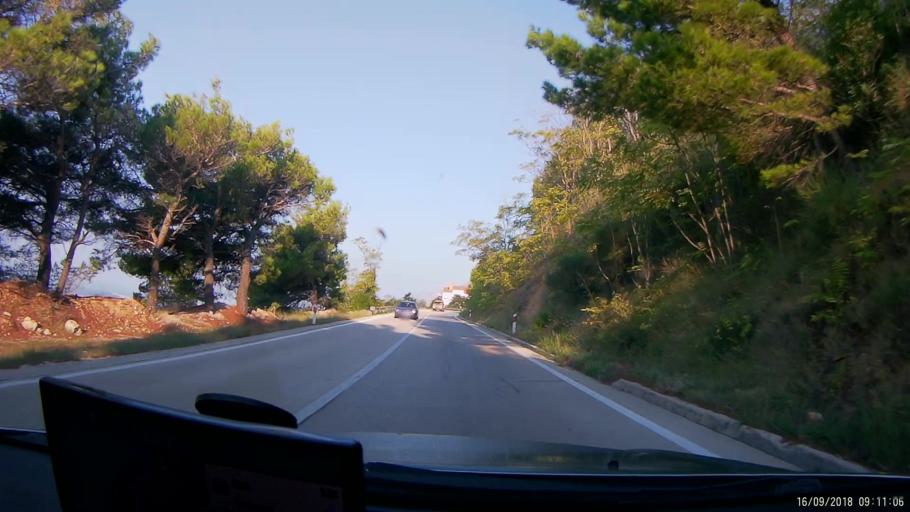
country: HR
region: Splitsko-Dalmatinska
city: Donja Brela
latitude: 43.3842
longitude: 16.9134
